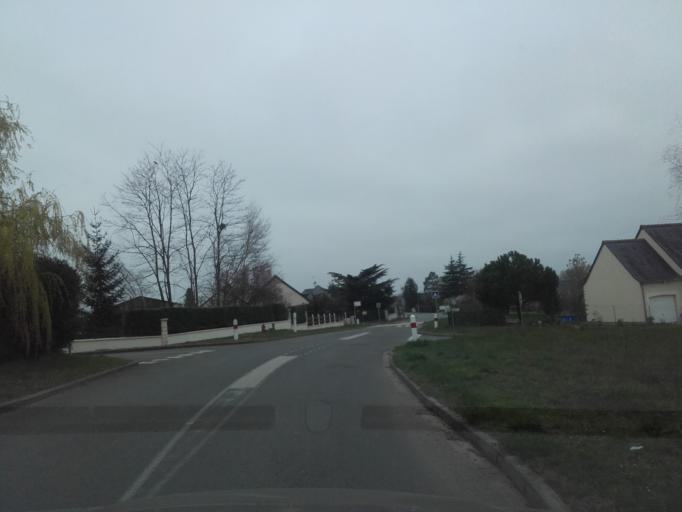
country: FR
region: Centre
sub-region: Departement d'Indre-et-Loire
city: Langeais
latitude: 47.3016
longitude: 0.4293
